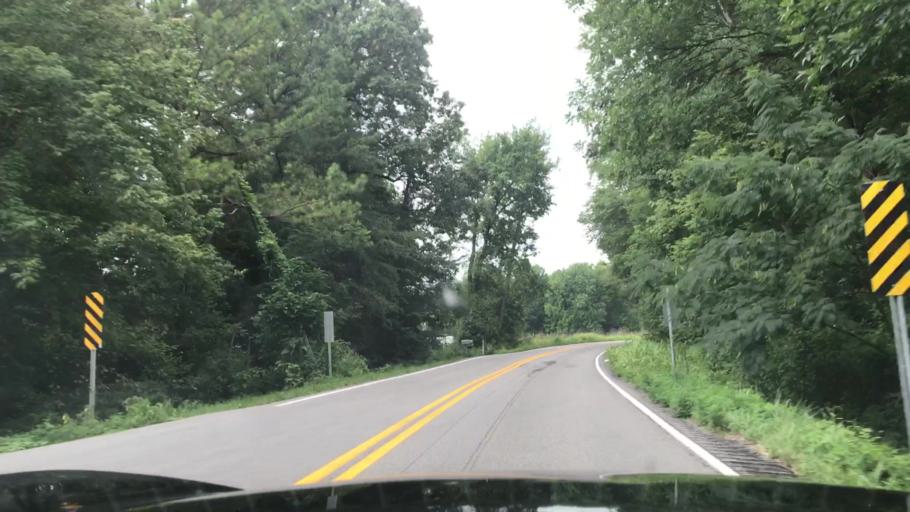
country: US
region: Kentucky
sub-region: Muhlenberg County
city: Central City
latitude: 37.1982
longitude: -87.0318
